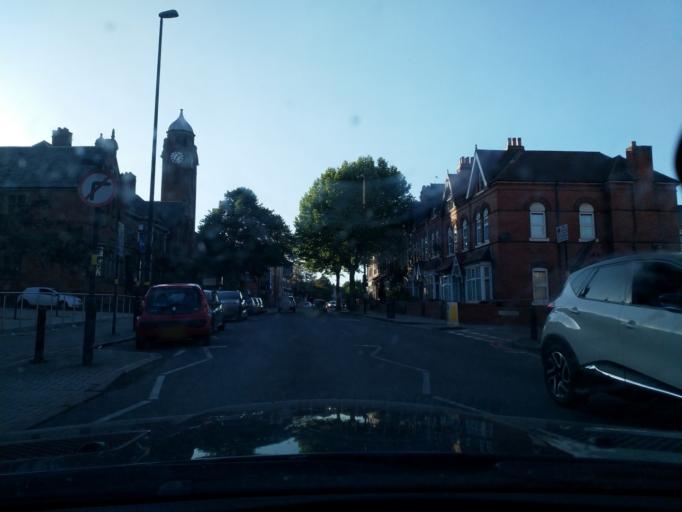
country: GB
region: England
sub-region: City and Borough of Birmingham
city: Acocks Green
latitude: 52.4501
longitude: -1.8635
